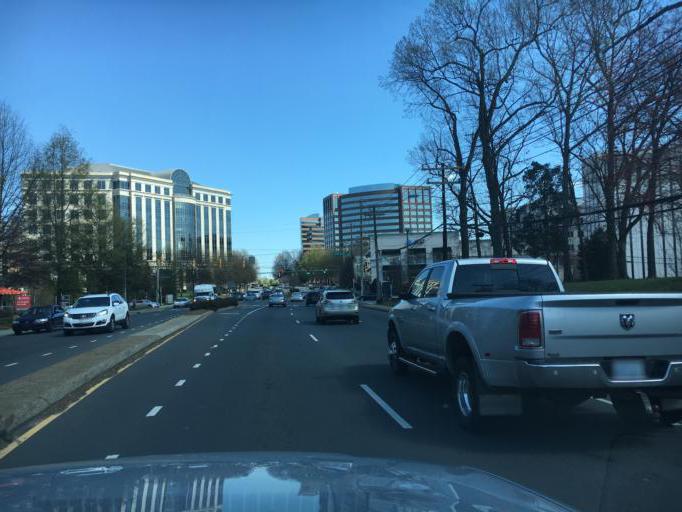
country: US
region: North Carolina
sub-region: Mecklenburg County
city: Charlotte
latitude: 35.1518
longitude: -80.8428
